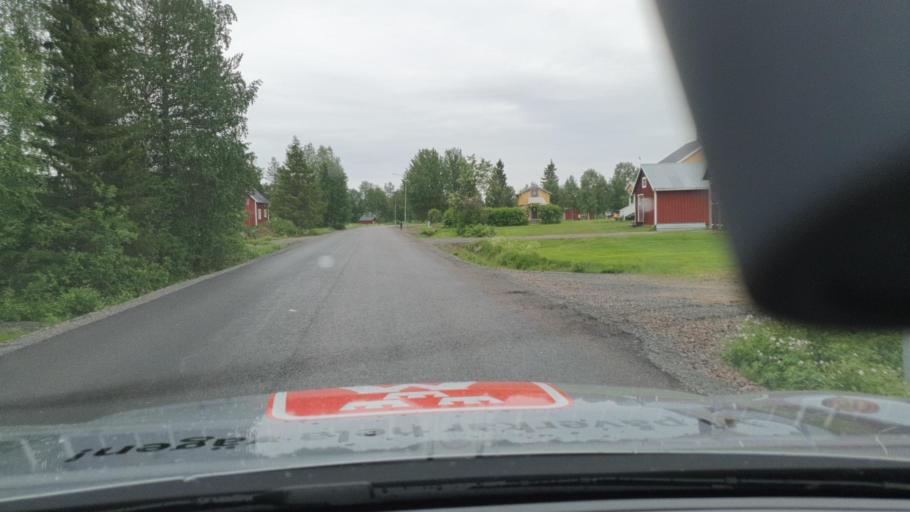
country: SE
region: Norrbotten
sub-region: Pajala Kommun
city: Pajala
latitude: 66.7342
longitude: 23.1725
